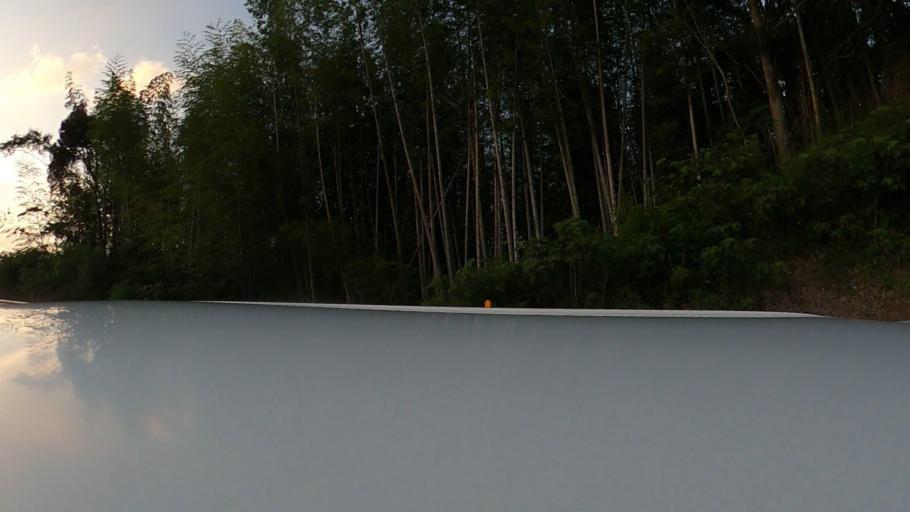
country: JP
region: Miyazaki
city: Nobeoka
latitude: 32.5756
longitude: 131.6203
